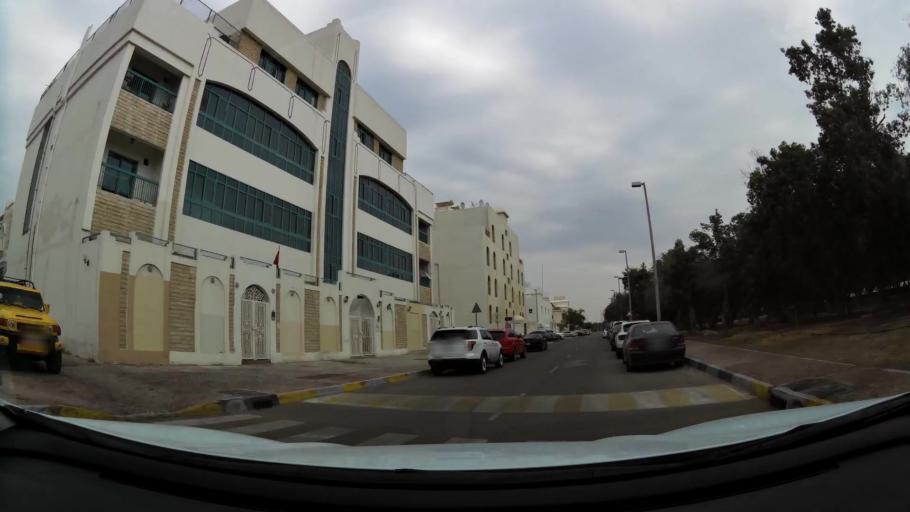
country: AE
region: Abu Dhabi
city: Abu Dhabi
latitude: 24.4422
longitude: 54.3981
